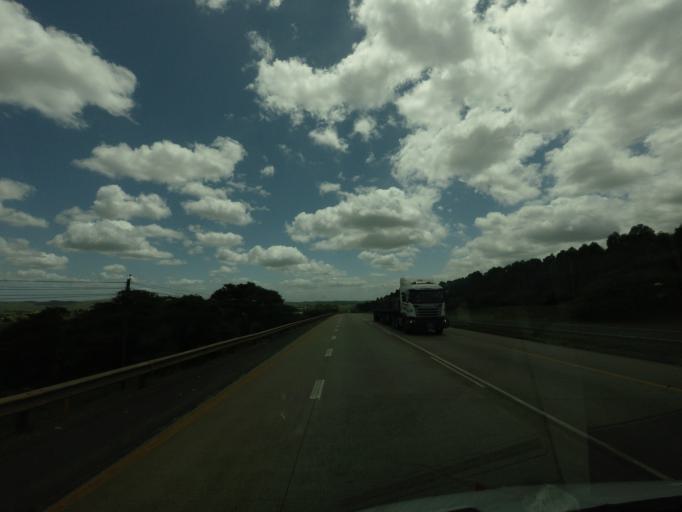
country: ZA
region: KwaZulu-Natal
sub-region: uMkhanyakude District Municipality
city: Mtubatuba
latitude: -28.4675
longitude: 32.1469
